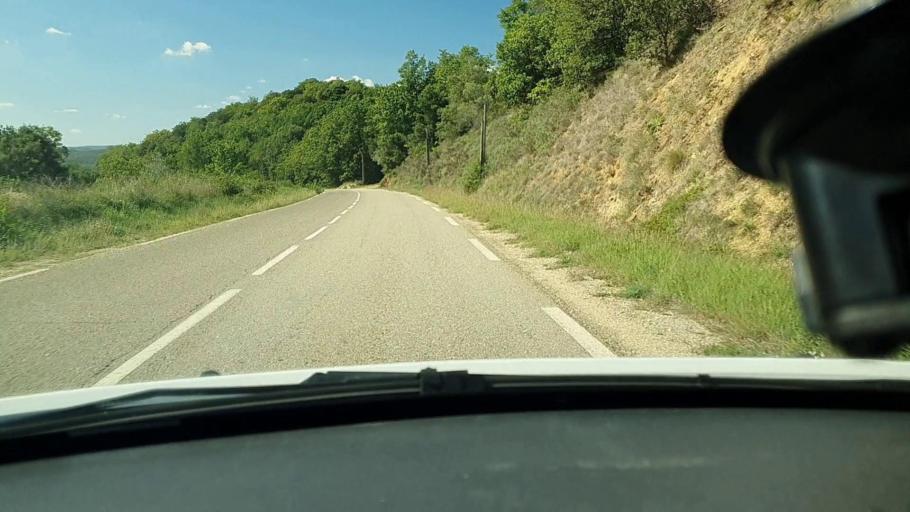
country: FR
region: Languedoc-Roussillon
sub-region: Departement du Gard
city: Sabran
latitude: 44.2194
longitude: 4.5398
